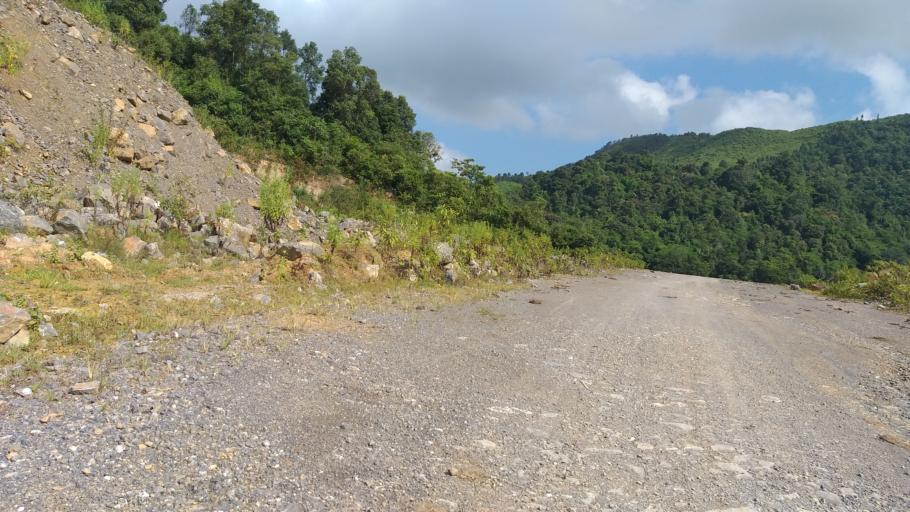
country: LA
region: Phongsali
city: Khoa
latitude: 21.2213
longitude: 102.5978
